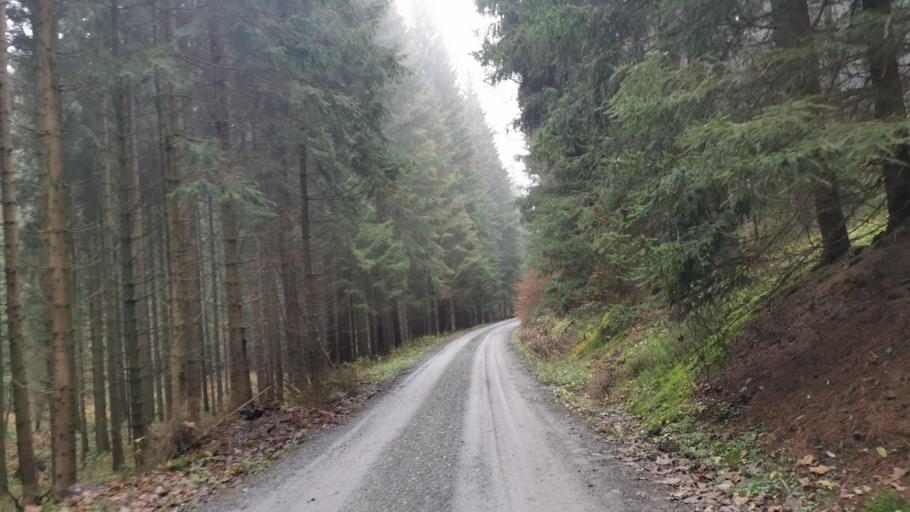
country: DE
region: Bavaria
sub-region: Upper Franconia
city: Ludwigsstadt
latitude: 50.4521
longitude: 11.3977
